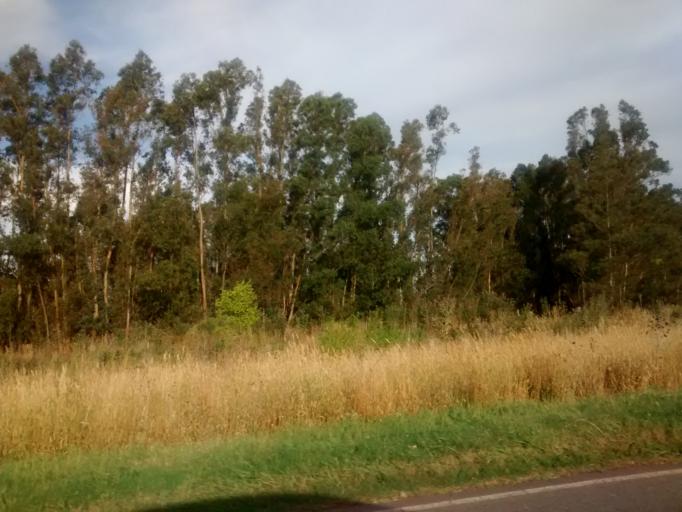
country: AR
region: Buenos Aires
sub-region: Partido de Loberia
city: Loberia
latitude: -38.2076
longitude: -58.7346
